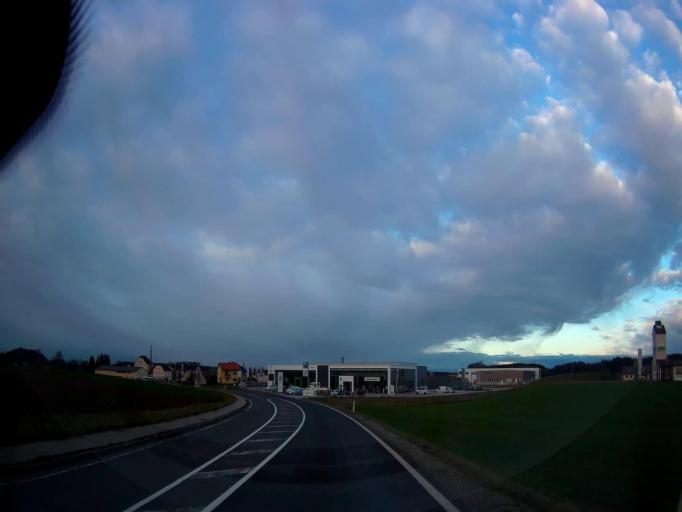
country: AT
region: Salzburg
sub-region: Politischer Bezirk Salzburg-Umgebung
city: Dorfbeuern
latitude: 48.0862
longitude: 12.9926
